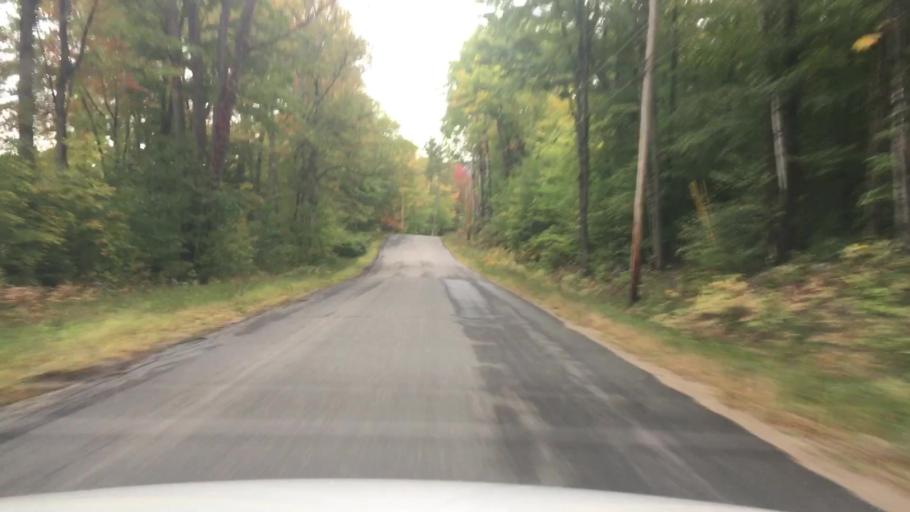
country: US
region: Maine
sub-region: Oxford County
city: Bethel
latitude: 44.4728
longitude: -70.7836
